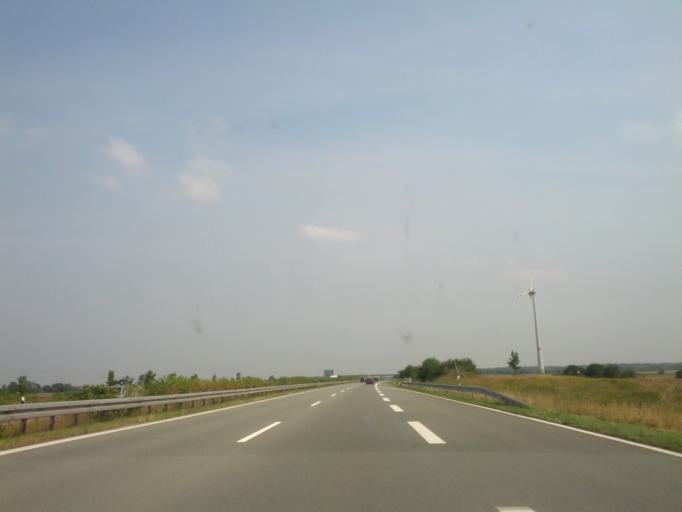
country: DE
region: Mecklenburg-Vorpommern
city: Tribsees
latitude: 54.0809
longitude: 12.7578
